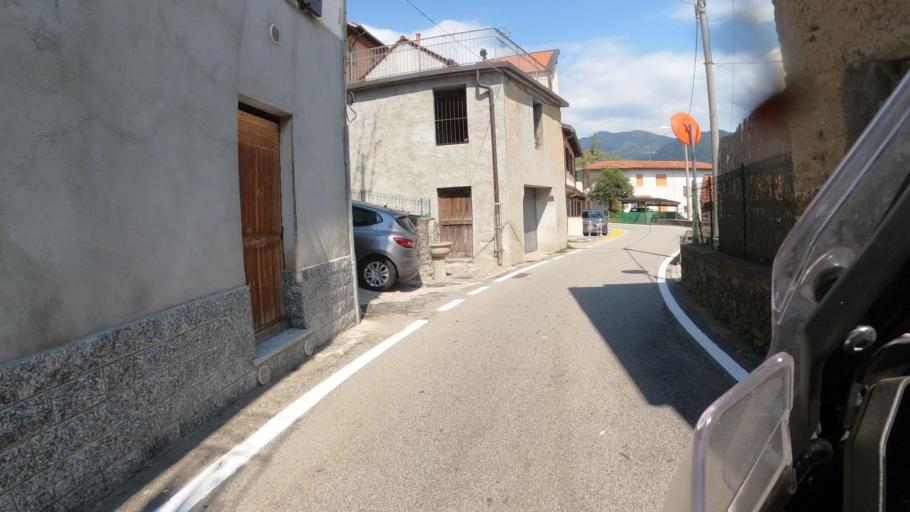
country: IT
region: Lombardy
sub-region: Provincia di Varese
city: Agra
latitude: 46.0536
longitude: 8.7656
